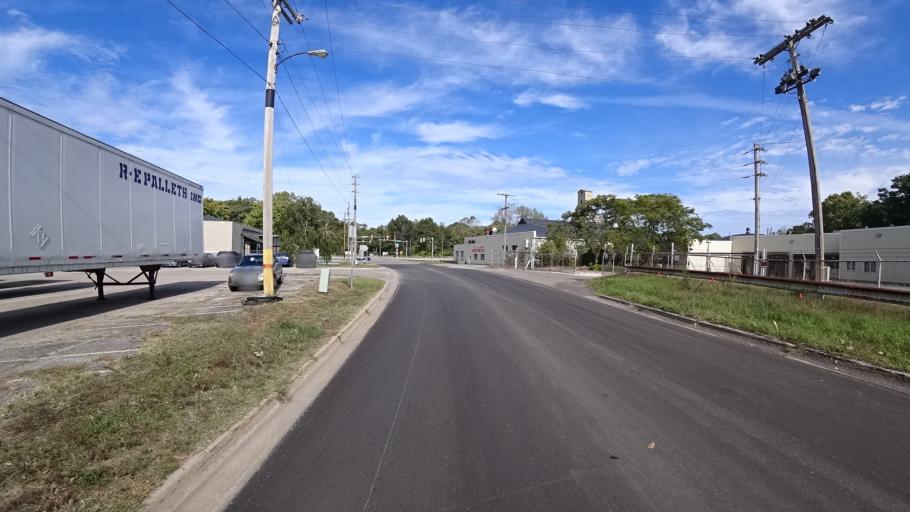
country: US
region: Indiana
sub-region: LaPorte County
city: Long Beach
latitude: 41.7244
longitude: -86.8759
